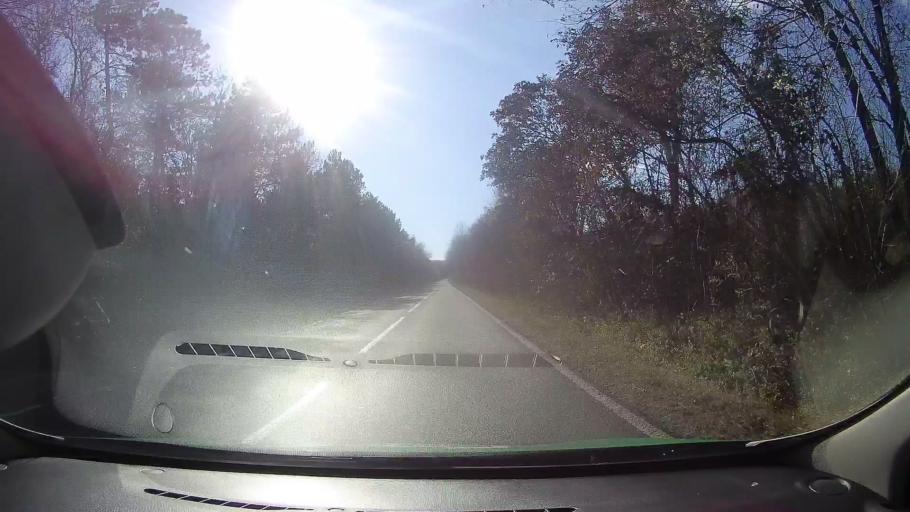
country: RO
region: Tulcea
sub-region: Oras Babadag
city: Babadag
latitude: 44.8365
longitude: 28.6954
